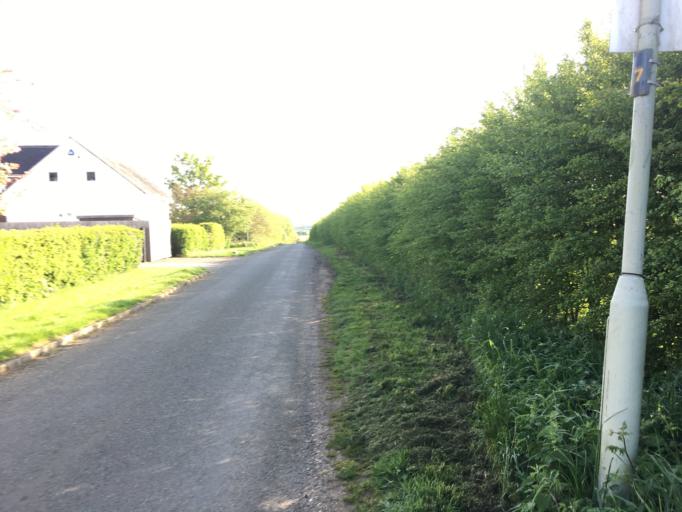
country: GB
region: England
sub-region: Leicestershire
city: Houghton on the Hill
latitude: 52.6285
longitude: -0.9936
